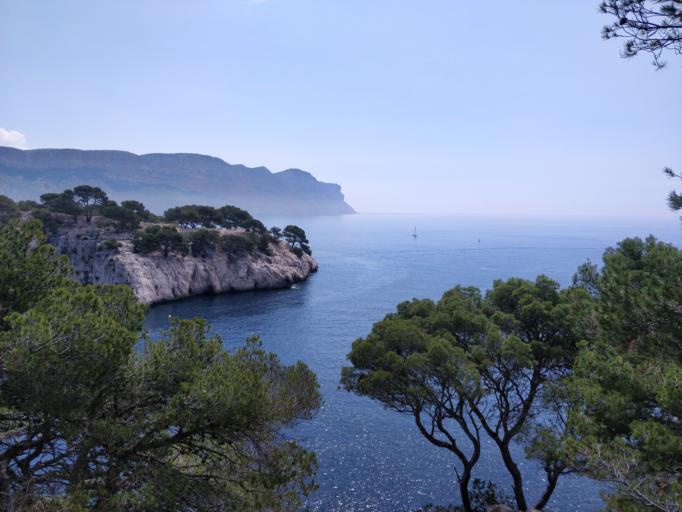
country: FR
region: Provence-Alpes-Cote d'Azur
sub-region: Departement des Bouches-du-Rhone
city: Cassis
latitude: 43.2045
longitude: 5.5118
